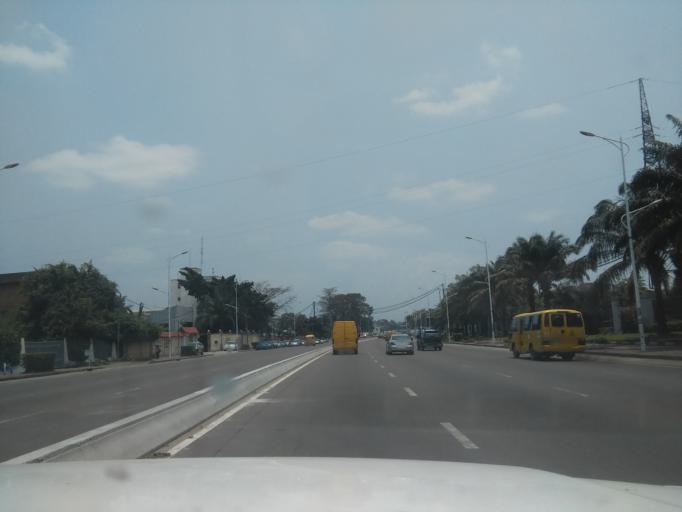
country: CD
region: Kinshasa
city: Kinshasa
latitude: -4.3183
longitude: 15.2773
